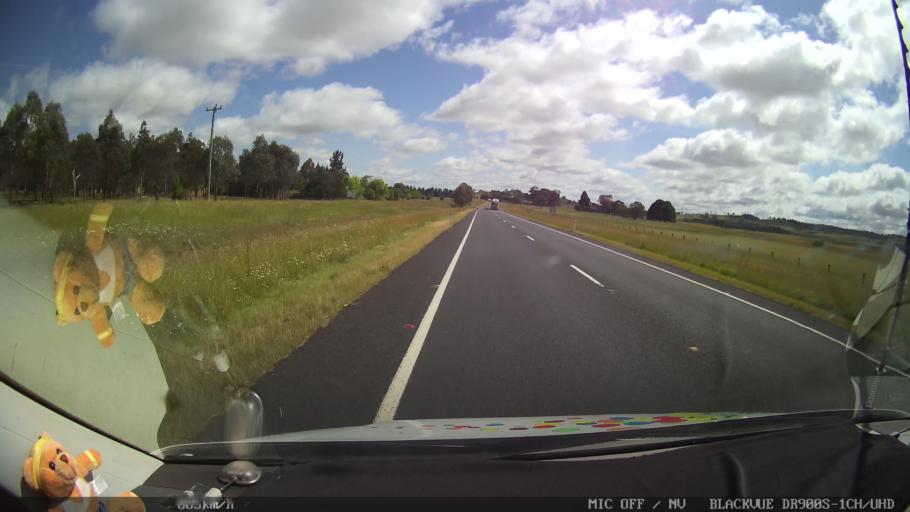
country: AU
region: New South Wales
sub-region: Glen Innes Severn
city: Glen Innes
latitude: -29.9150
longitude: 151.7288
